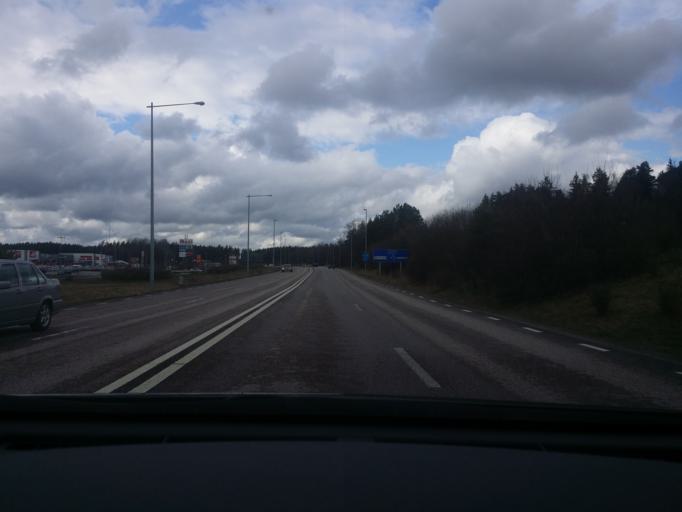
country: SE
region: Vaestmanland
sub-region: Vasteras
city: Vasteras
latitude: 59.6159
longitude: 16.4674
